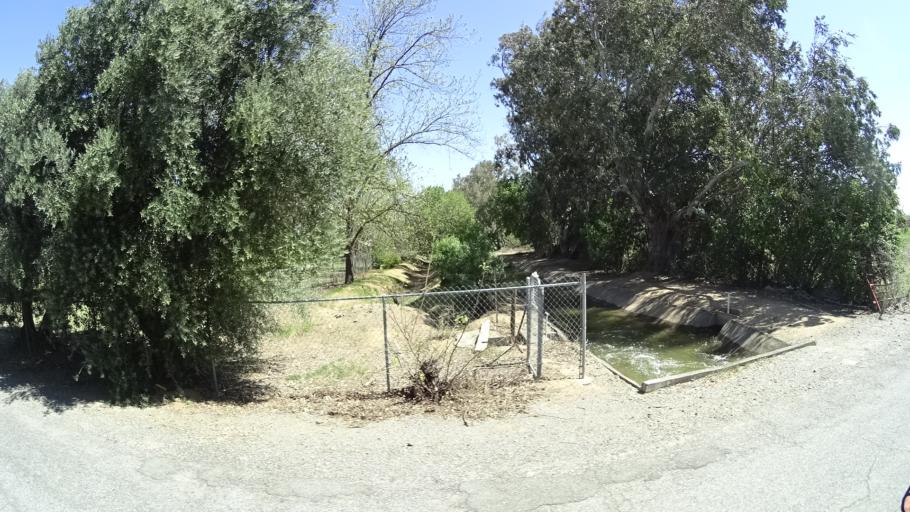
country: US
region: California
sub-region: Glenn County
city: Orland
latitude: 39.7727
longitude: -122.1783
